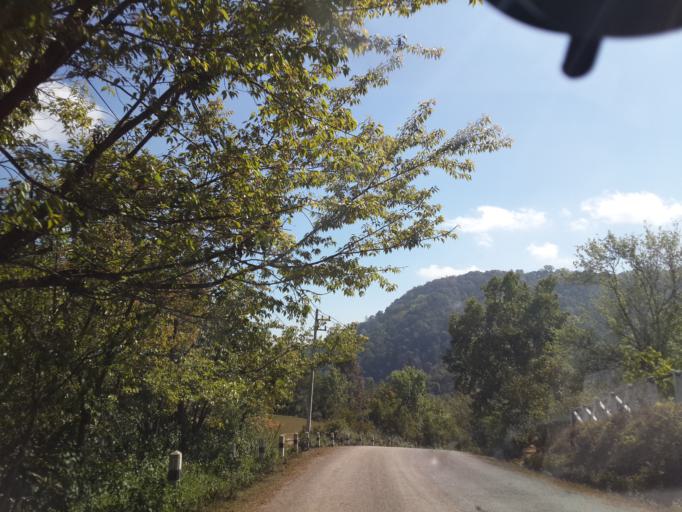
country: TH
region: Chiang Mai
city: Fang
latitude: 19.9077
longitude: 99.0535
